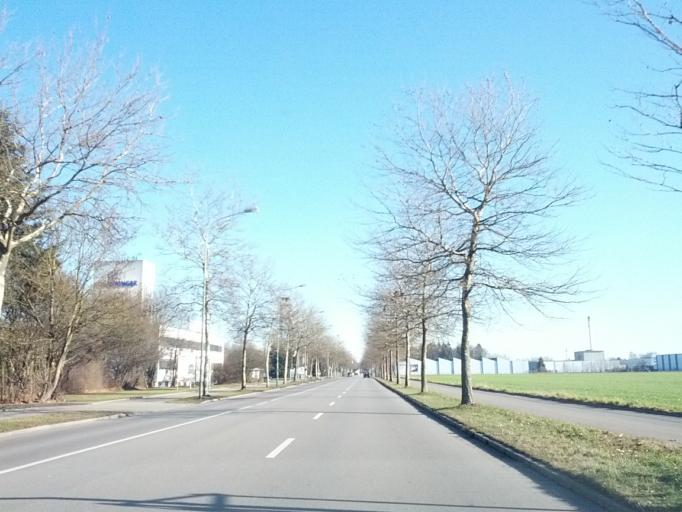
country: DE
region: Bavaria
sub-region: Swabia
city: Memmingen
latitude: 47.9955
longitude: 10.1672
